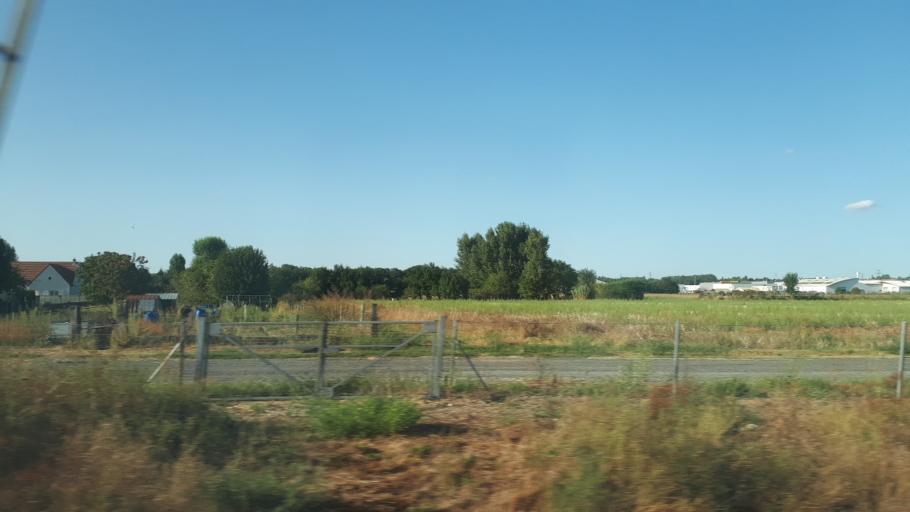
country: FR
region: Centre
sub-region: Departement d'Indre-et-Loire
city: La Ville-aux-Dames
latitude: 47.3906
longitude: 0.7810
